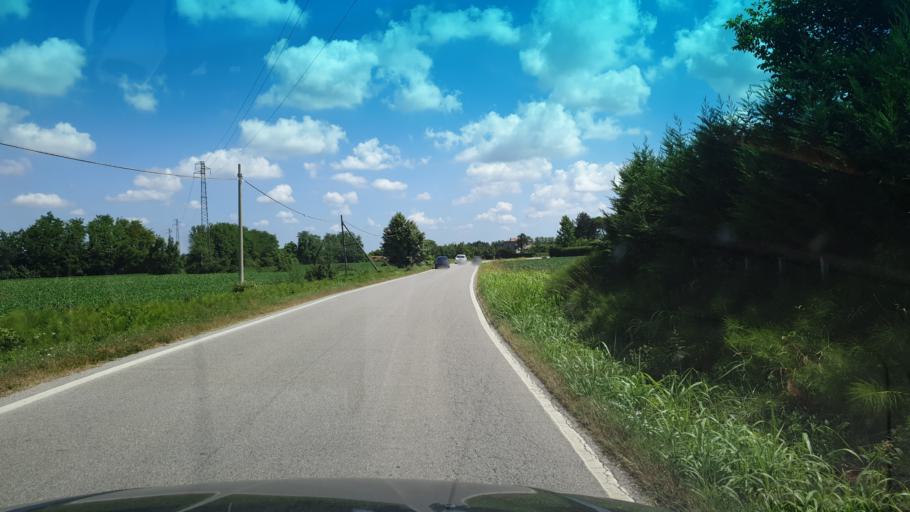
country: IT
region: Veneto
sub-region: Provincia di Rovigo
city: Costa di Rovigo
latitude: 45.0680
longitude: 11.7167
